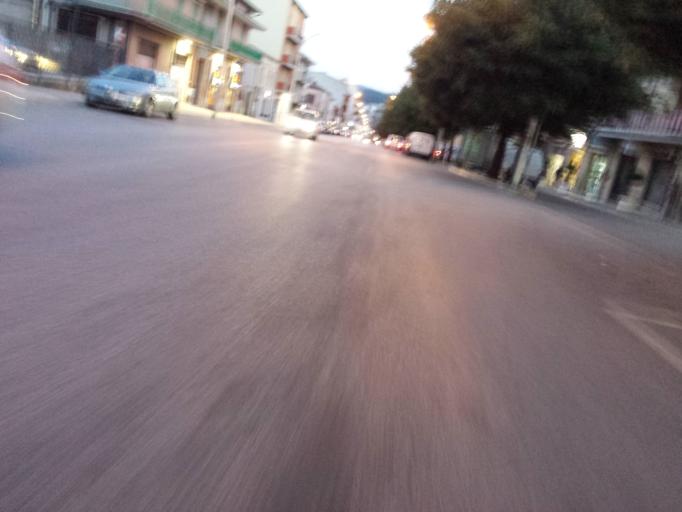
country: IT
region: Molise
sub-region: Provincia di Campobasso
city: Campobasso
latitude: 41.5666
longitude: 14.6724
